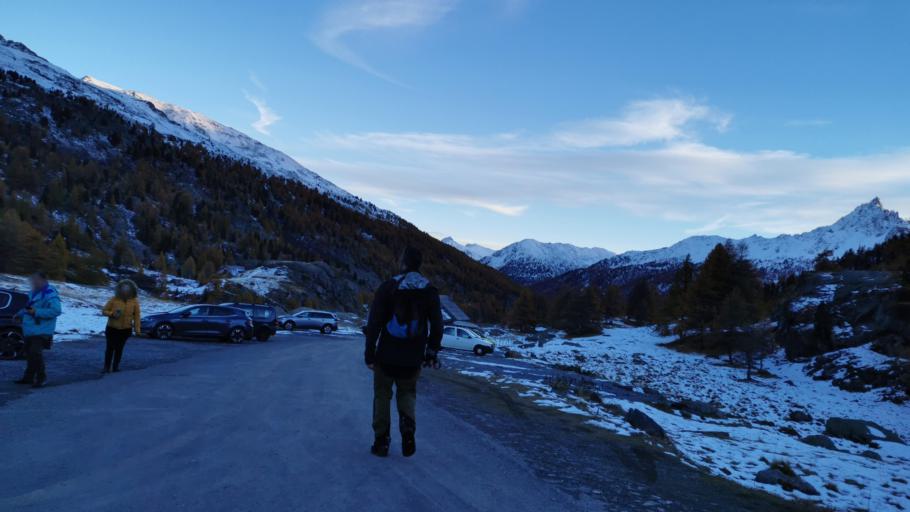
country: FR
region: Provence-Alpes-Cote d'Azur
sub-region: Departement des Hautes-Alpes
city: Le Monetier-les-Bains
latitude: 45.0592
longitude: 6.5257
